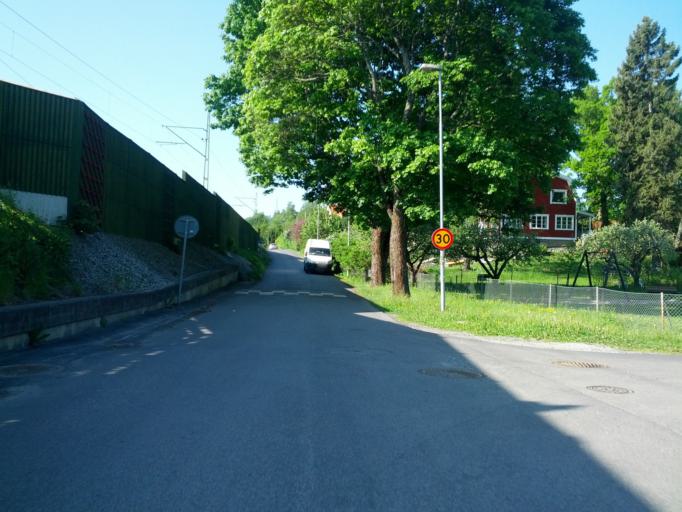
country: SE
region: Stockholm
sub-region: Taby Kommun
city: Taby
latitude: 59.4323
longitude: 18.0524
